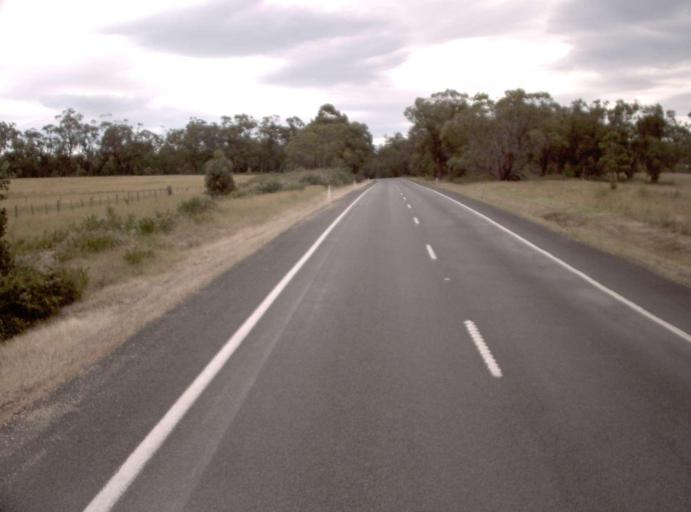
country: AU
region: Victoria
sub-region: Wellington
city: Sale
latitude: -38.2745
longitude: 147.0353
